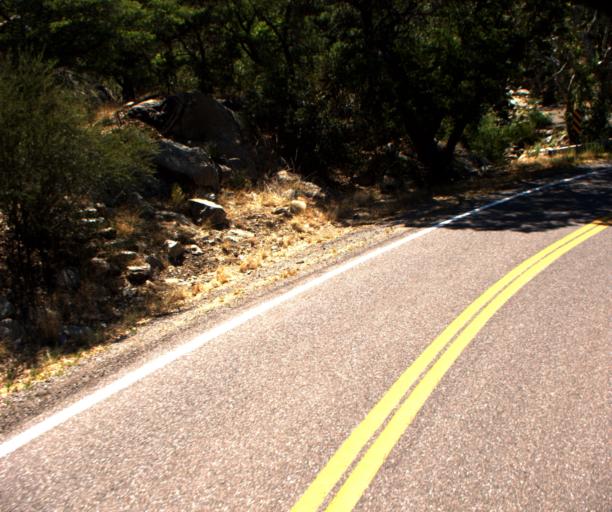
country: US
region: Arizona
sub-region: Graham County
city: Swift Trail Junction
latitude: 32.6673
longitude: -109.7968
